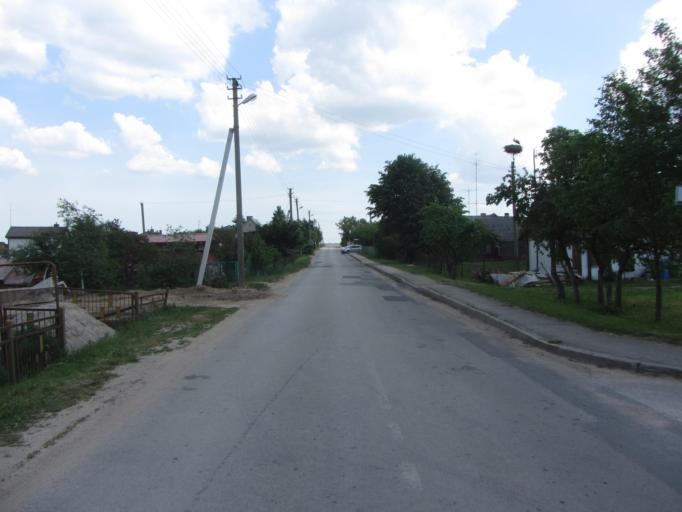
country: LT
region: Kauno apskritis
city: Jonava
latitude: 54.9829
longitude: 24.1985
